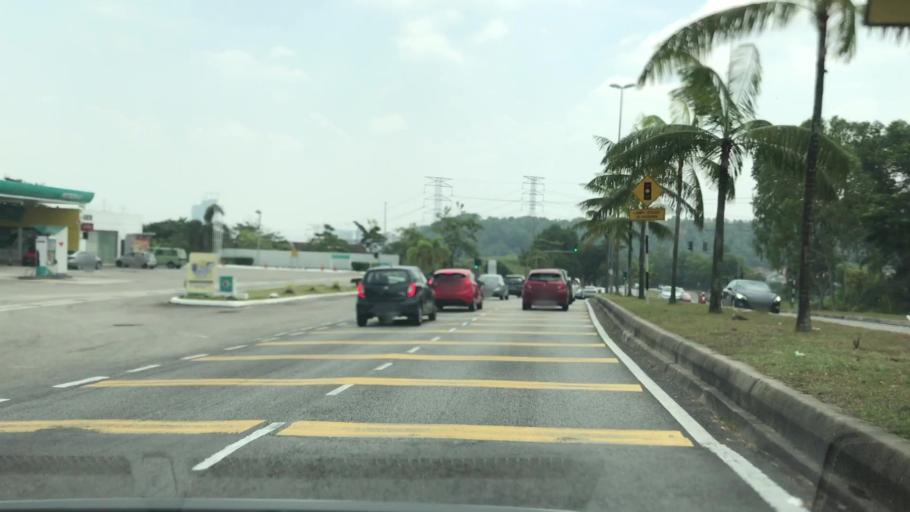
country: MY
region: Selangor
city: Kampong Baharu Balakong
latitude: 3.0267
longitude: 101.6803
